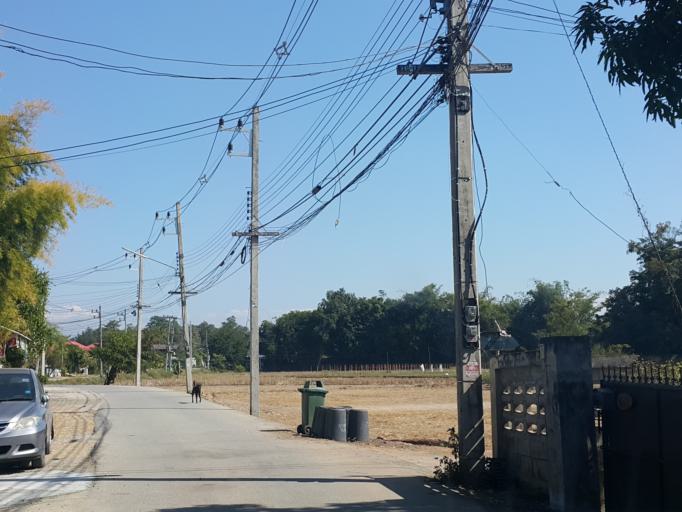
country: TH
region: Chiang Mai
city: San Sai
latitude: 18.8523
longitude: 98.9970
